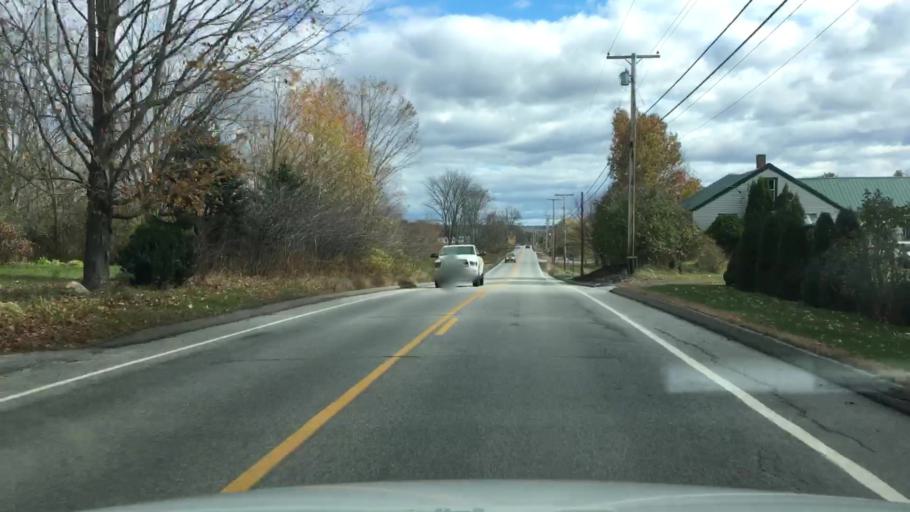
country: US
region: Maine
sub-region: Sagadahoc County
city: Richmond
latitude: 44.0928
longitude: -69.8319
